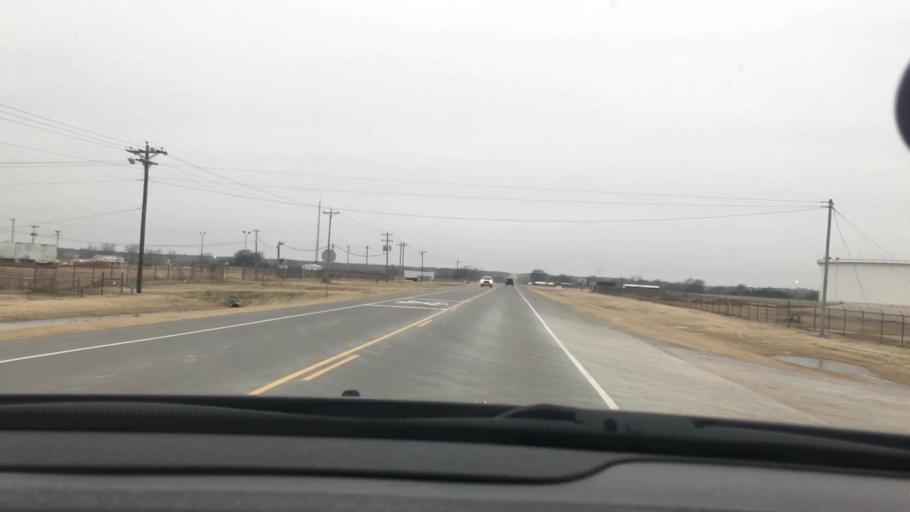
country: US
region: Oklahoma
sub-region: Garvin County
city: Wynnewood
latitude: 34.6227
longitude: -97.1704
